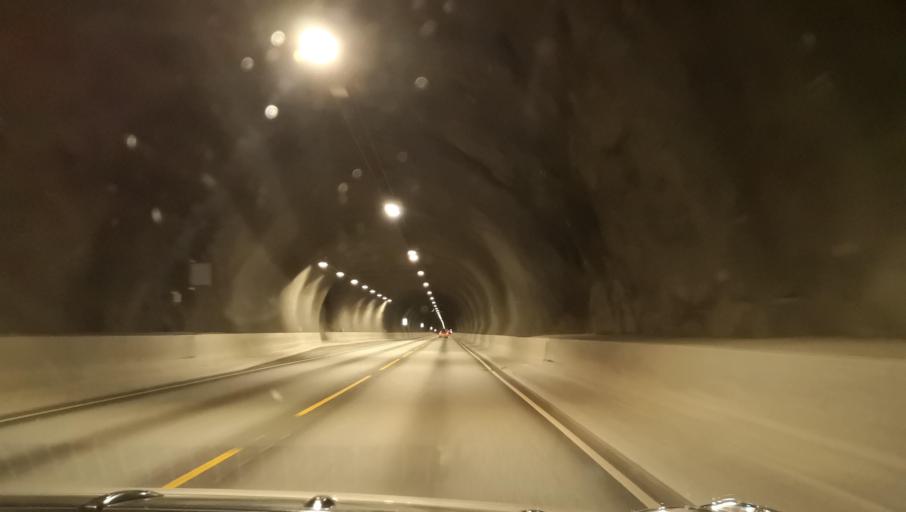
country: NO
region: Hordaland
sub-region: Granvin
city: Granvin
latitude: 60.5736
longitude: 6.6994
